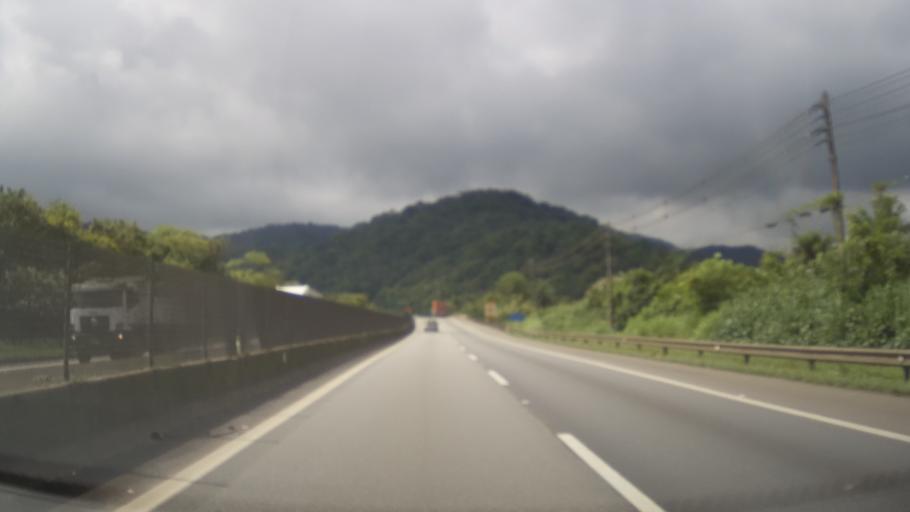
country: BR
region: Sao Paulo
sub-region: Cubatao
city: Cubatao
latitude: -23.8653
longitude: -46.3463
